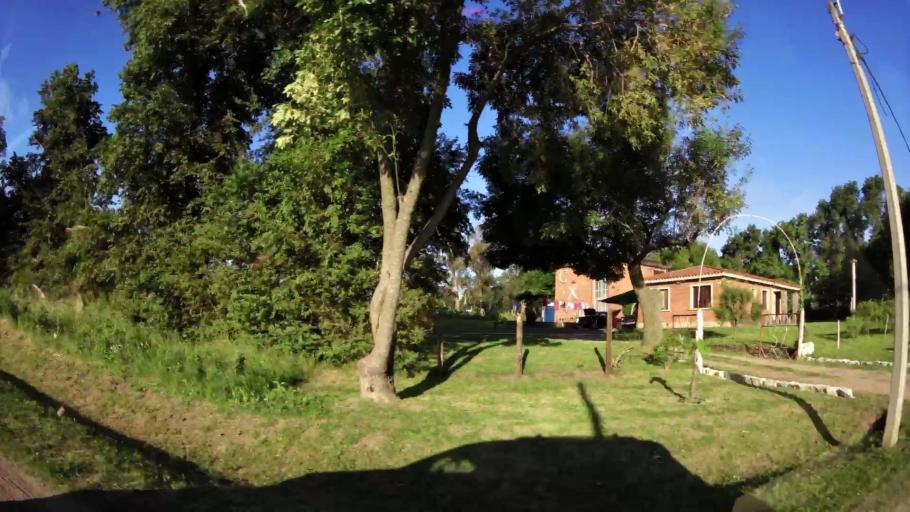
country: UY
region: Canelones
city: La Paz
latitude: -34.8283
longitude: -56.2455
